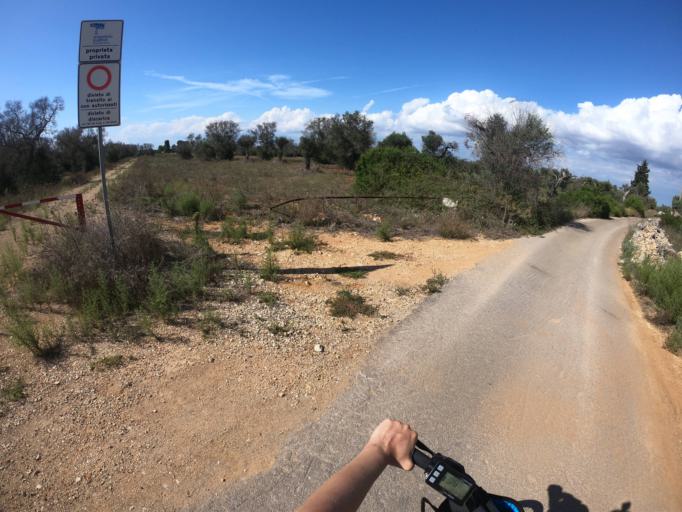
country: IT
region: Apulia
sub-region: Provincia di Lecce
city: Galatone
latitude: 40.1366
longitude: 18.0583
